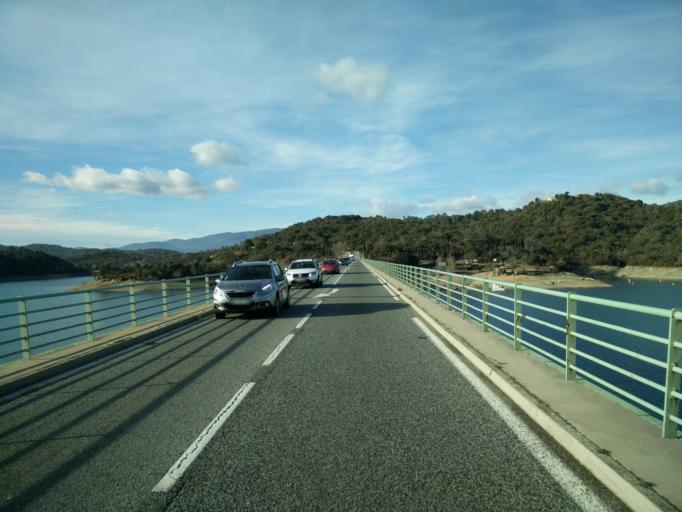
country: FR
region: Provence-Alpes-Cote d'Azur
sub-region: Departement du Var
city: Montauroux
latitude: 43.5824
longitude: 6.8040
